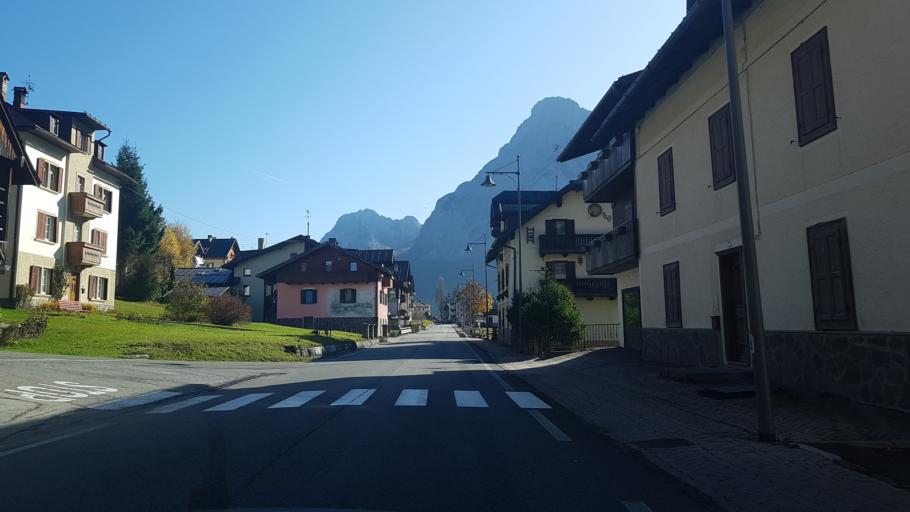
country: IT
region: Veneto
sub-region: Provincia di Belluno
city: Sappada
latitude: 46.5655
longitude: 12.6684
